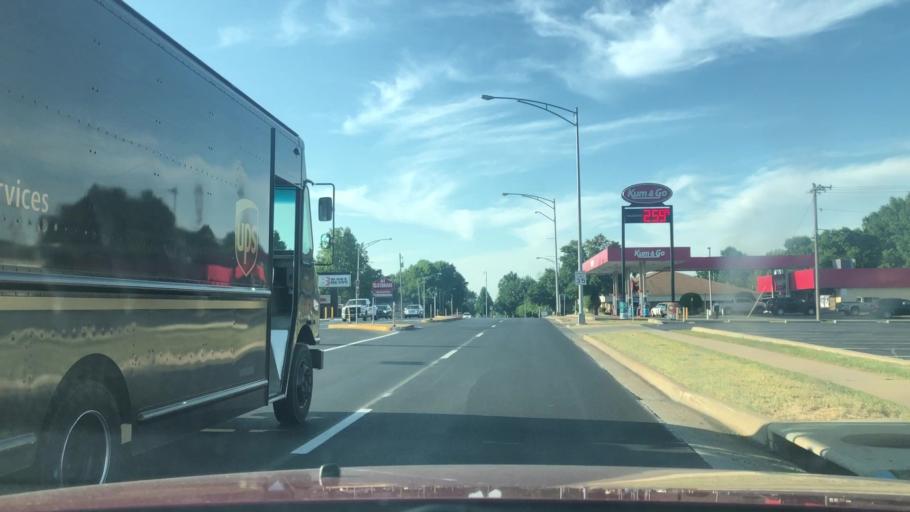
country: US
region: Missouri
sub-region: Greene County
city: Springfield
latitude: 37.1603
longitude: -93.2771
